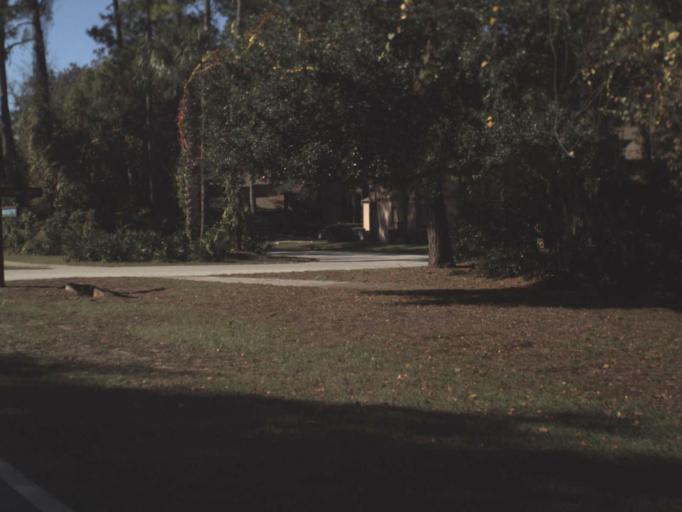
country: US
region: Florida
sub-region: Flagler County
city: Palm Coast
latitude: 29.5625
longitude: -81.1945
